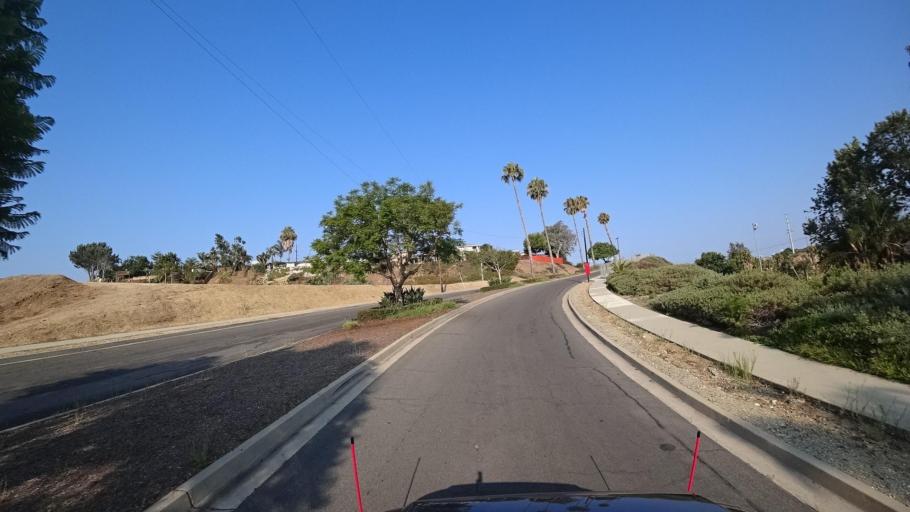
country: US
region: California
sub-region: San Diego County
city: Oceanside
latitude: 33.2108
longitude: -117.3812
